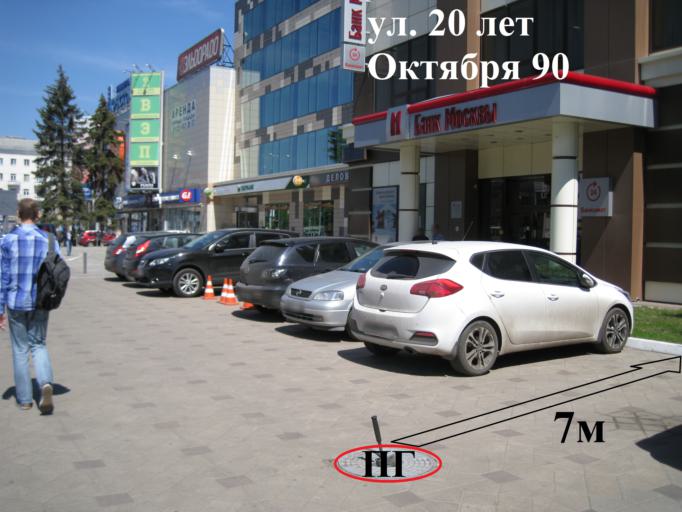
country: RU
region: Voronezj
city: Voronezh
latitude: 51.6545
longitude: 39.1893
